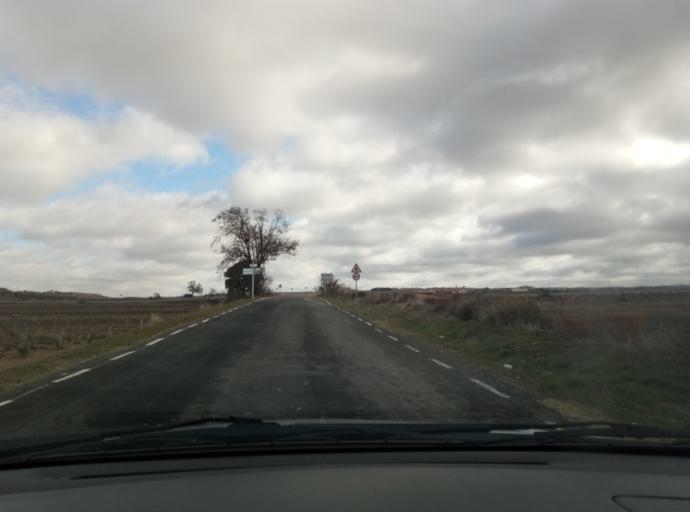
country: ES
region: Catalonia
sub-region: Provincia de Lleida
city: Verdu
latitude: 41.6107
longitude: 1.1102
